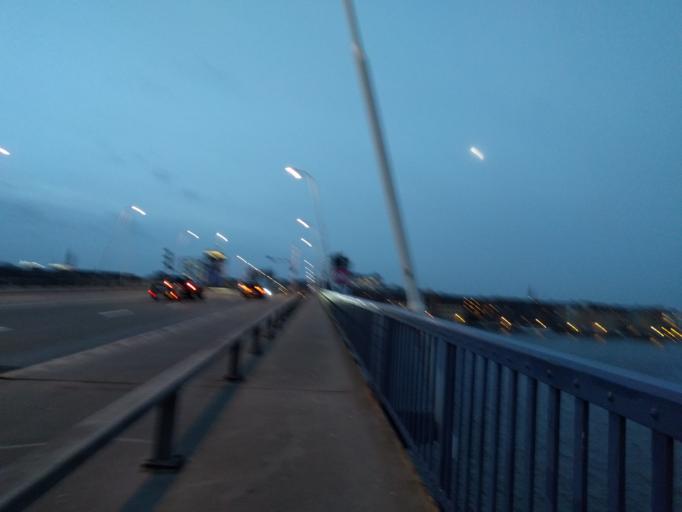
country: DK
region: North Denmark
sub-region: Alborg Kommune
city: Aalborg
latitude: 57.0554
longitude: 9.9203
